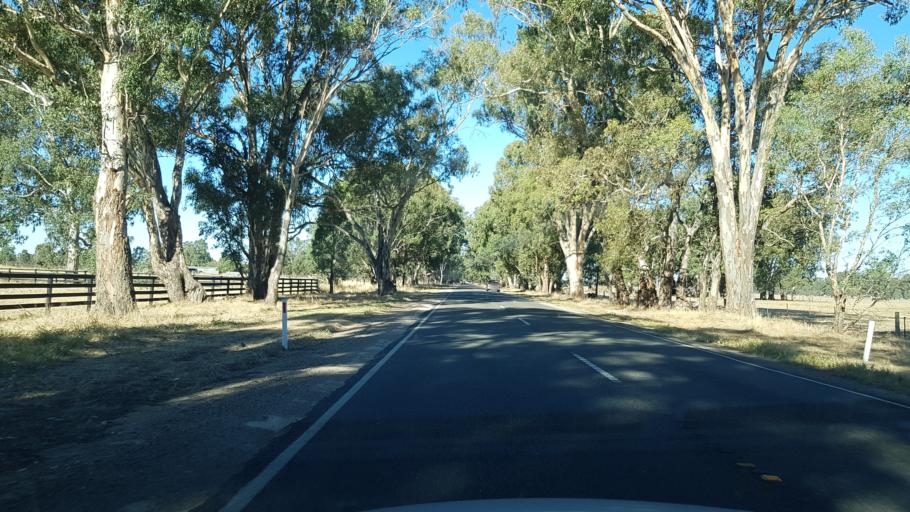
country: AU
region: Victoria
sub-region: Wangaratta
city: Wangaratta
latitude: -36.4337
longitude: 146.3059
